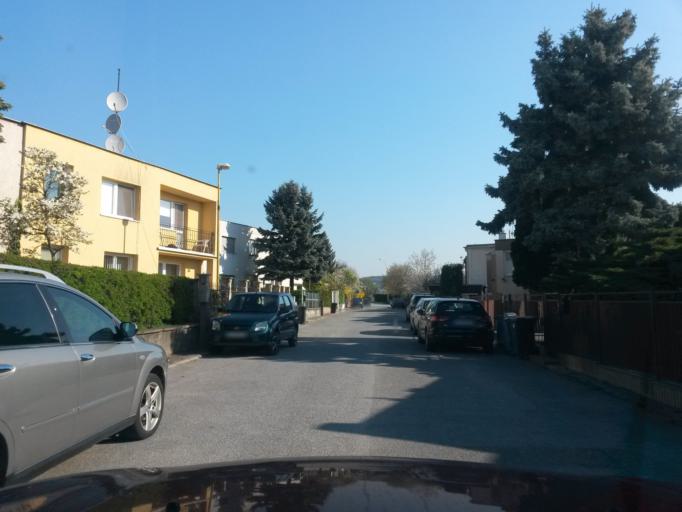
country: SK
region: Kosicky
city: Kosice
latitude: 48.7498
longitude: 21.2453
